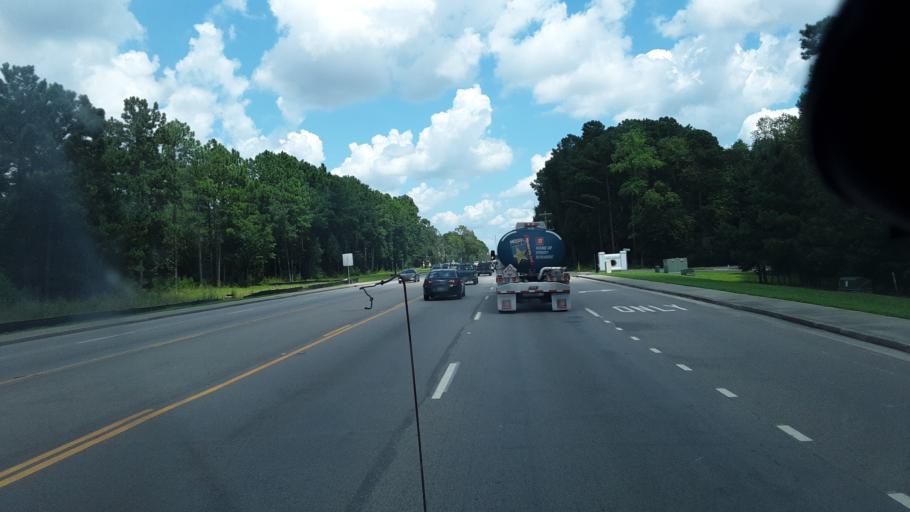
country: US
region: South Carolina
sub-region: Berkeley County
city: Sangaree
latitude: 33.0602
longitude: -80.0961
